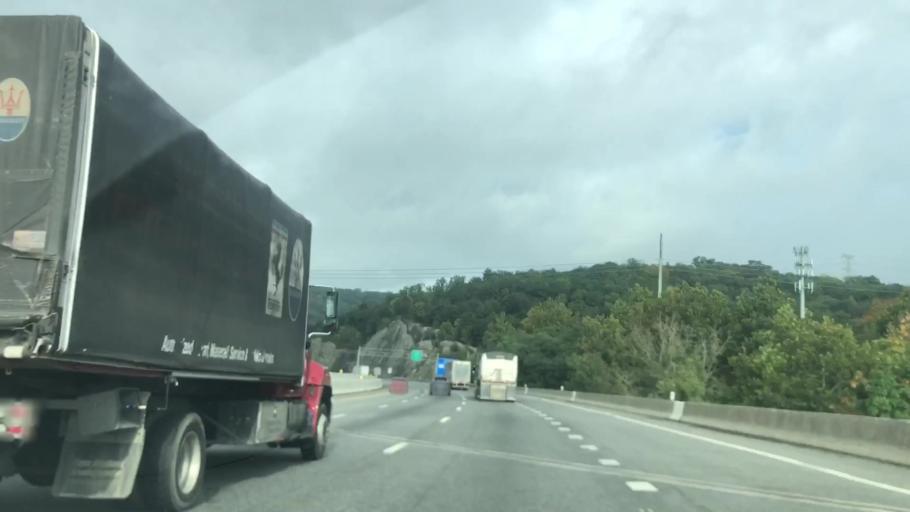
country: US
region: New York
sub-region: Rockland County
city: Sloatsburg
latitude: 41.1397
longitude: -74.1702
